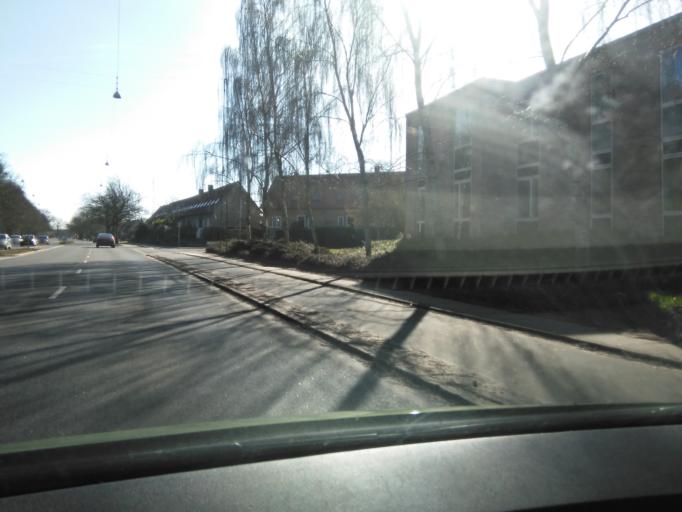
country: DK
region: Central Jutland
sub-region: Arhus Kommune
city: Arhus
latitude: 56.1825
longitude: 10.2178
